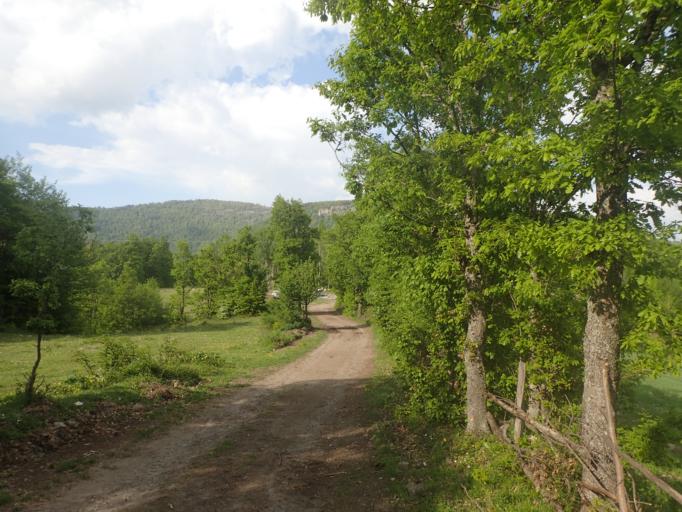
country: TR
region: Ordu
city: Akkus
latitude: 40.8213
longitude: 36.9340
